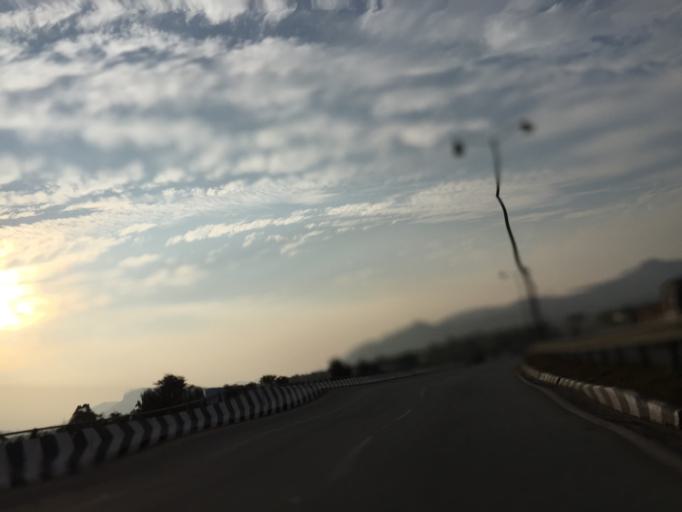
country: IN
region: Karnataka
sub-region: Kolar
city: Kolar
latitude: 13.1153
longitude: 78.1366
